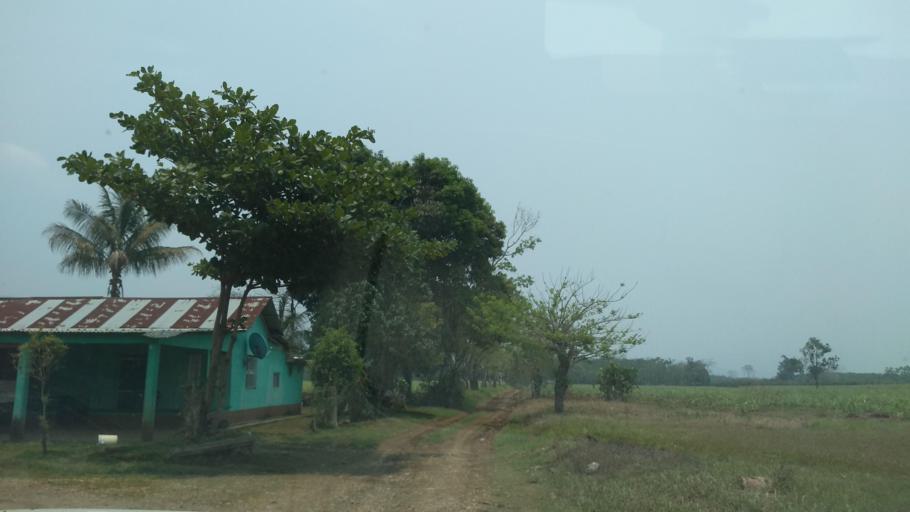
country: MX
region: Veracruz
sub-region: Tezonapa
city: Laguna Chica (Pueblo Nuevo)
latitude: 18.5114
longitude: -96.7360
